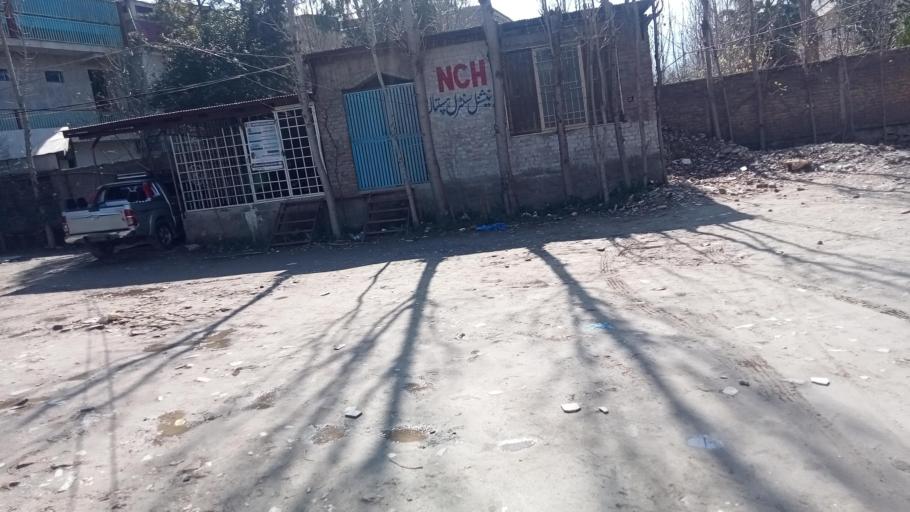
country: PK
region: Khyber Pakhtunkhwa
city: Saidu Sharif
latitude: 34.7606
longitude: 72.3570
